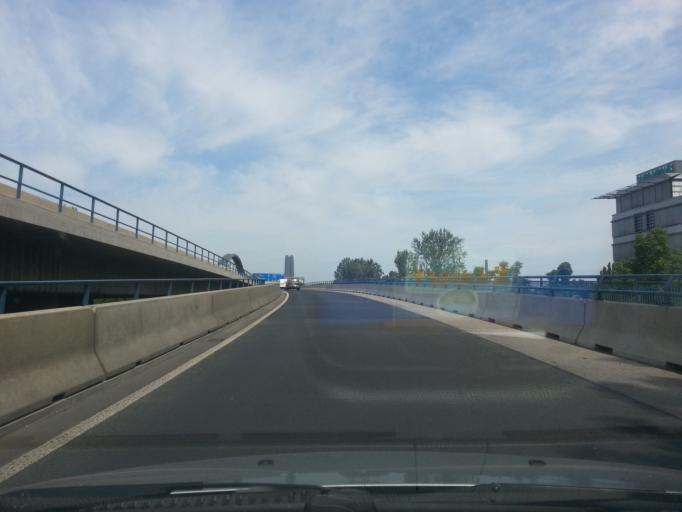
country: DE
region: Hesse
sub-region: Regierungsbezirk Darmstadt
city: Offenbach
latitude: 50.1081
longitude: 8.7378
